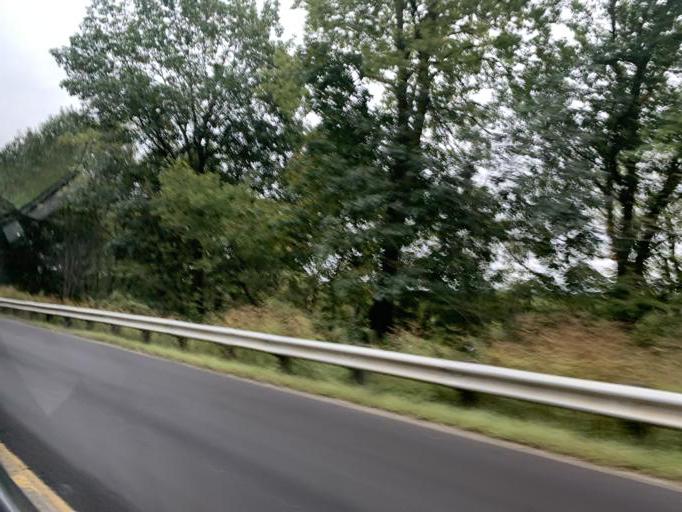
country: US
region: Wisconsin
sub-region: Grant County
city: Muscoda
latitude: 43.2020
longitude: -90.4318
